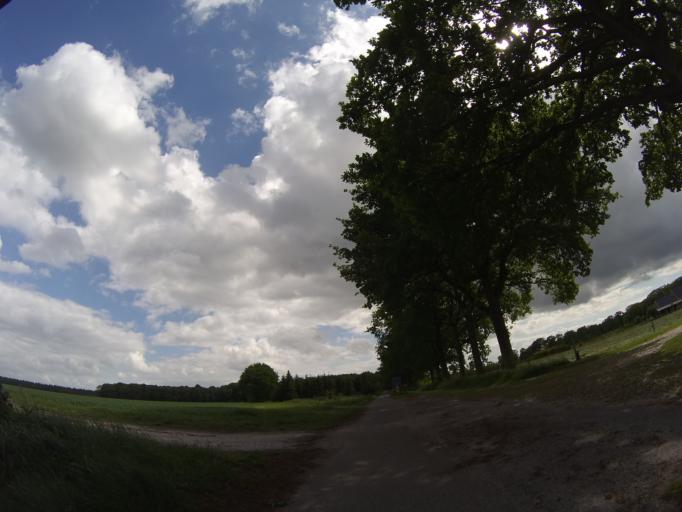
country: NL
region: Drenthe
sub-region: Gemeente Borger-Odoorn
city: Borger
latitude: 52.8736
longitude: 6.8659
